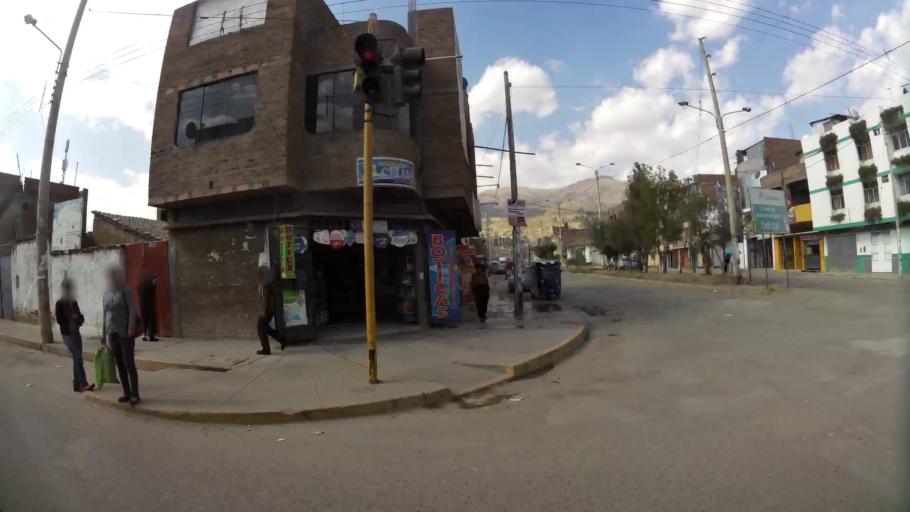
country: PE
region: Junin
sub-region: Provincia de Huancayo
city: Huancayo
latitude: -12.0858
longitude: -75.1996
